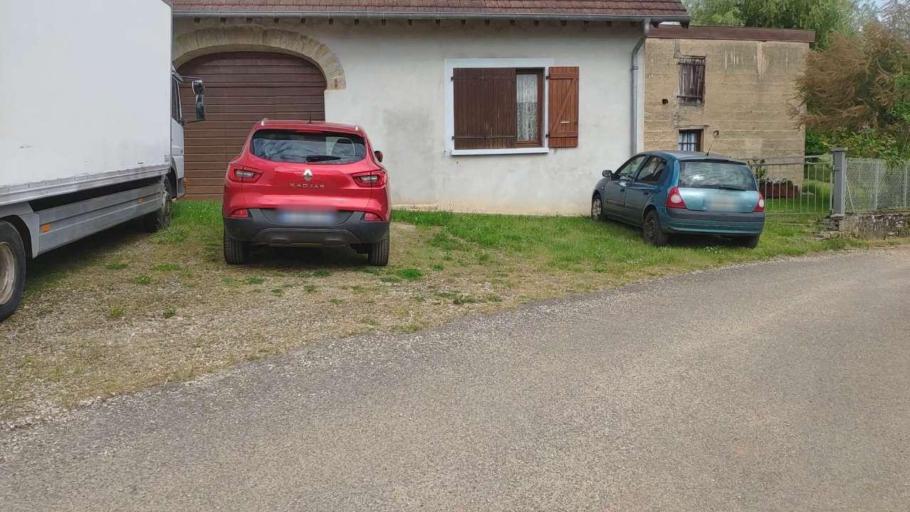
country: FR
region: Franche-Comte
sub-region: Departement du Jura
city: Bletterans
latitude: 46.7947
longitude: 5.5590
